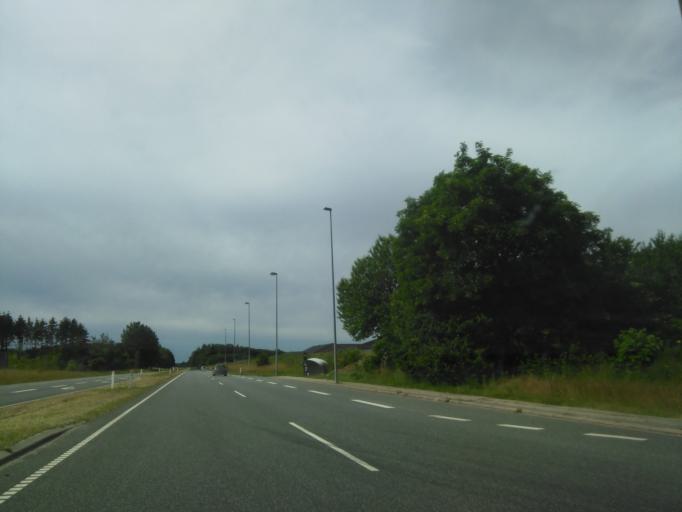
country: DK
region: Central Jutland
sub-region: Arhus Kommune
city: Tranbjerg
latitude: 56.0845
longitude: 10.1219
